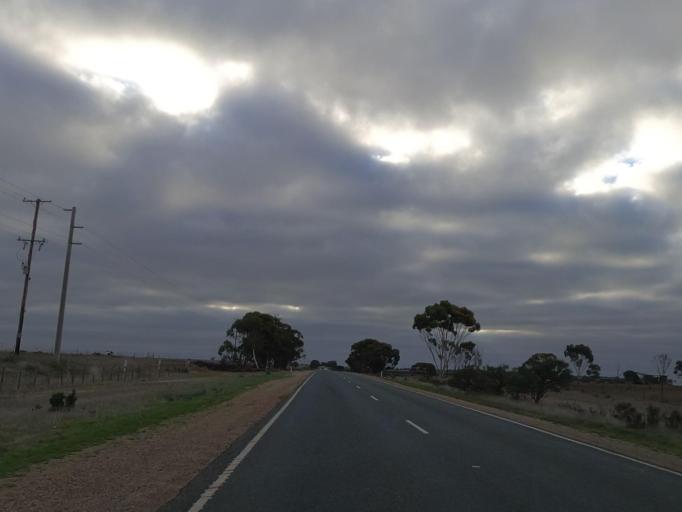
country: AU
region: Victoria
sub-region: Swan Hill
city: Swan Hill
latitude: -35.6410
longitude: 143.8291
